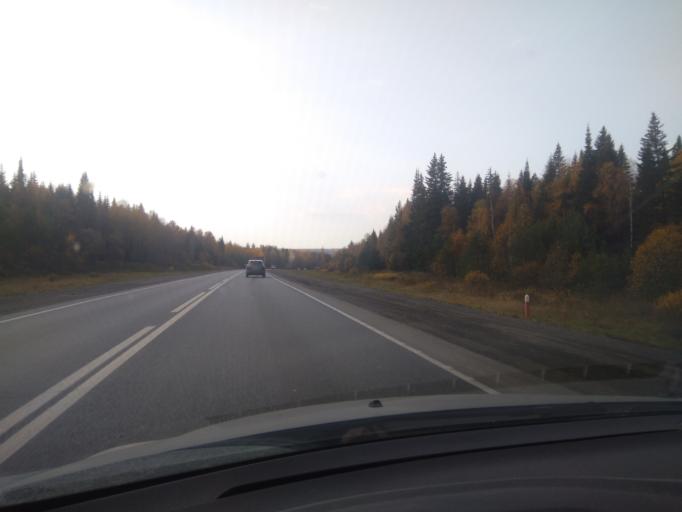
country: RU
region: Sverdlovsk
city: Druzhinino
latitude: 56.8144
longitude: 59.5596
